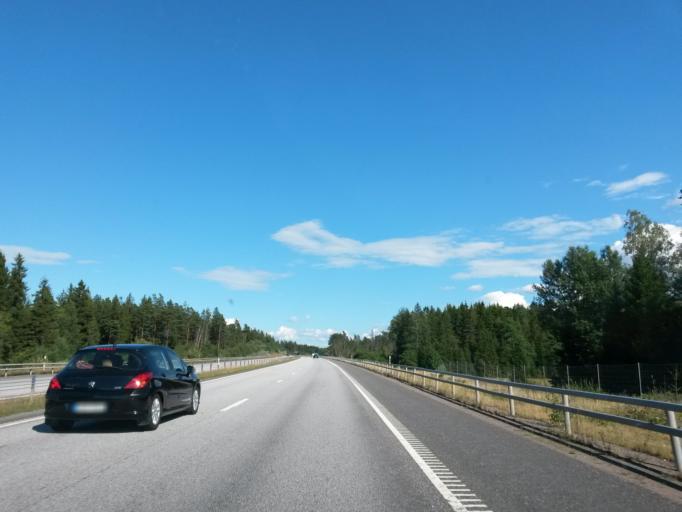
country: SE
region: Vaestra Goetaland
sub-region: Uddevalla Kommun
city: Uddevalla
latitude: 58.3338
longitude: 12.0044
